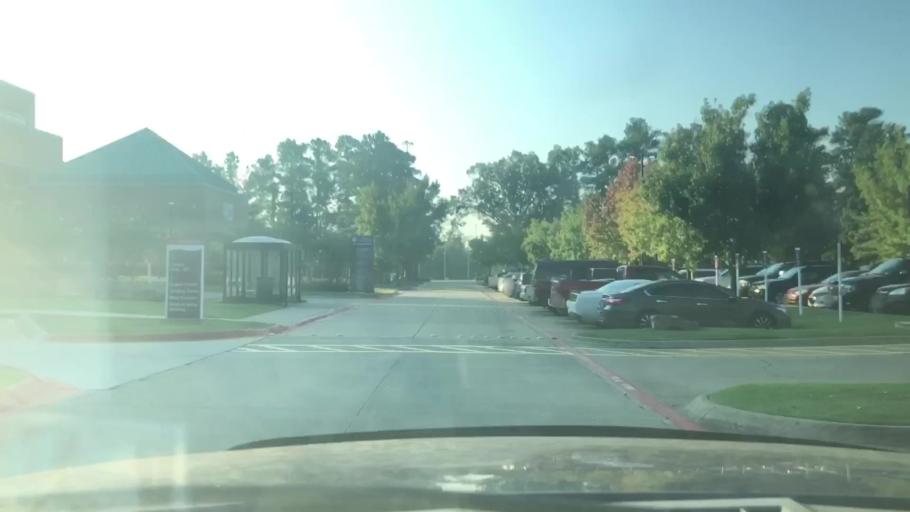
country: US
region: Arkansas
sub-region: Miller County
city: Texarkana
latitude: 33.4635
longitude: -94.0762
